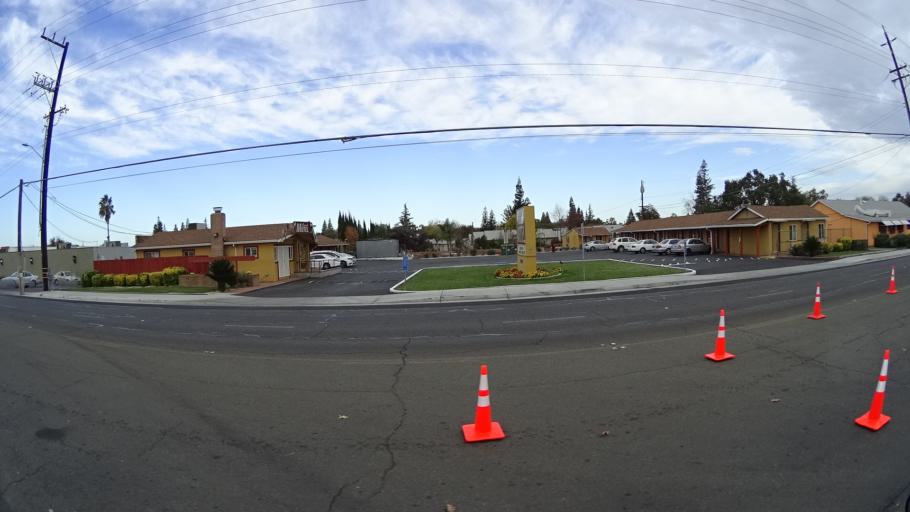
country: US
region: California
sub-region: Sacramento County
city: Antelope
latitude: 38.6801
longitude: -121.3189
